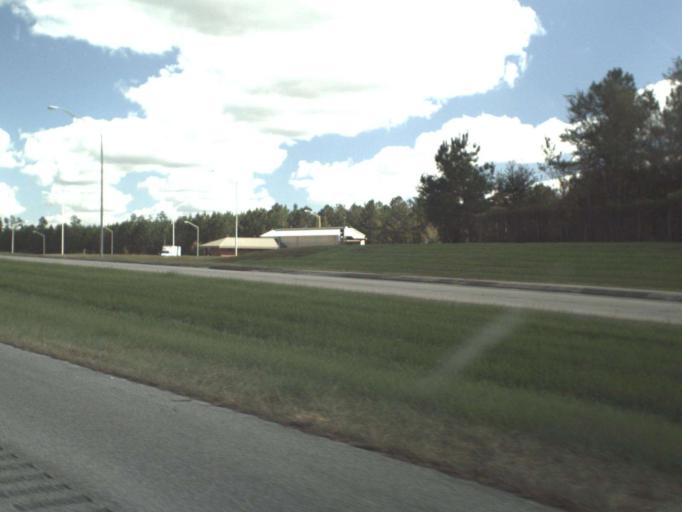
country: US
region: Florida
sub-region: Jackson County
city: Sneads
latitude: 30.6387
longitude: -84.9868
